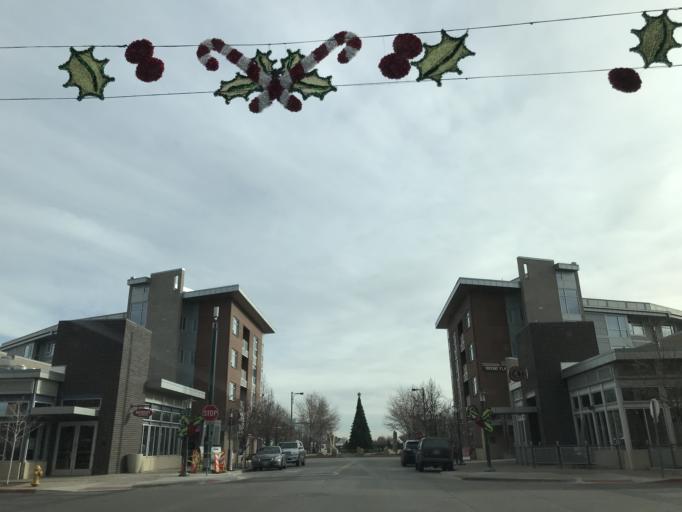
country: US
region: Colorado
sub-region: Adams County
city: Commerce City
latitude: 39.7580
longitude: -104.9019
